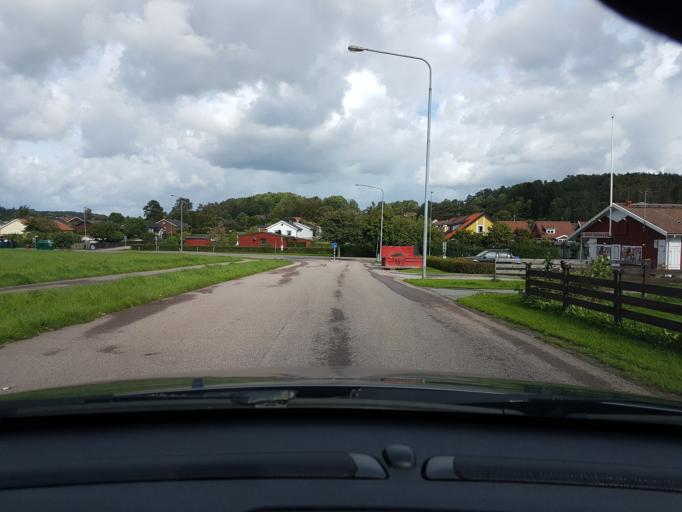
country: SE
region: Vaestra Goetaland
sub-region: Ale Kommun
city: Nodinge-Nol
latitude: 57.9076
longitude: 12.0560
